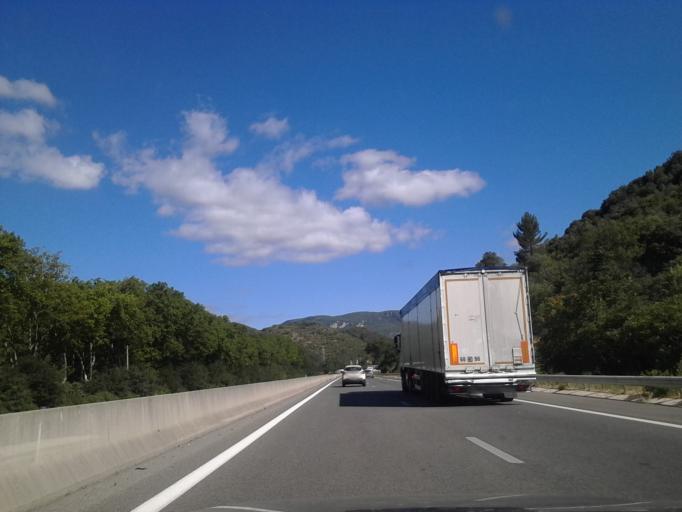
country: FR
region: Languedoc-Roussillon
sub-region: Departement de l'Herault
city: Lodeve
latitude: 43.7084
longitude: 3.3266
